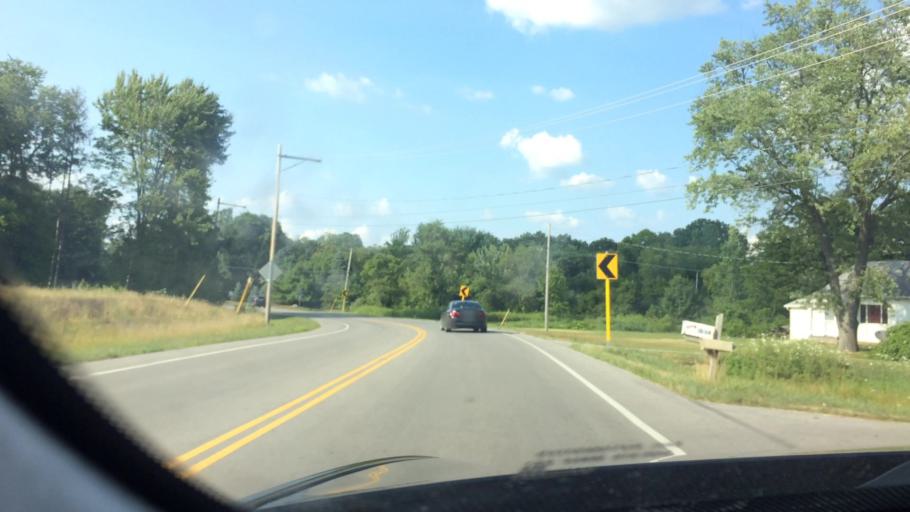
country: US
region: Ohio
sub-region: Lucas County
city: Holland
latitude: 41.6547
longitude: -83.7226
